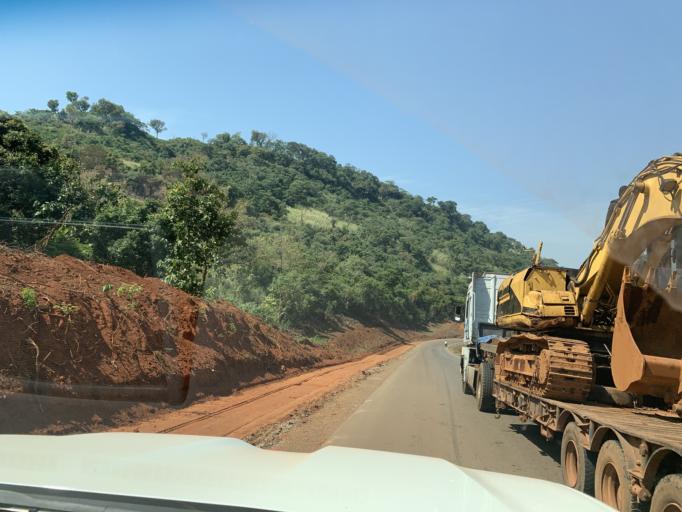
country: GN
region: Mamou
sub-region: Mamou Prefecture
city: Mamou
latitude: 10.1988
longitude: -12.4660
